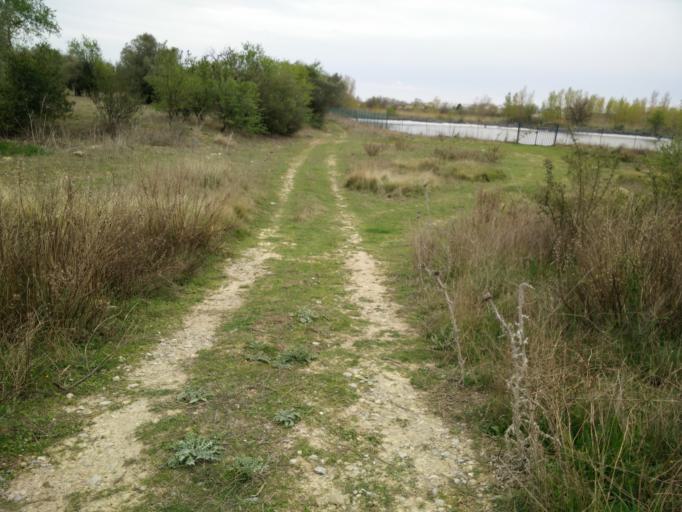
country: FR
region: Languedoc-Roussillon
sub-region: Departement du Gard
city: Gallargues-le-Montueux
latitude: 43.7135
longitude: 4.1690
